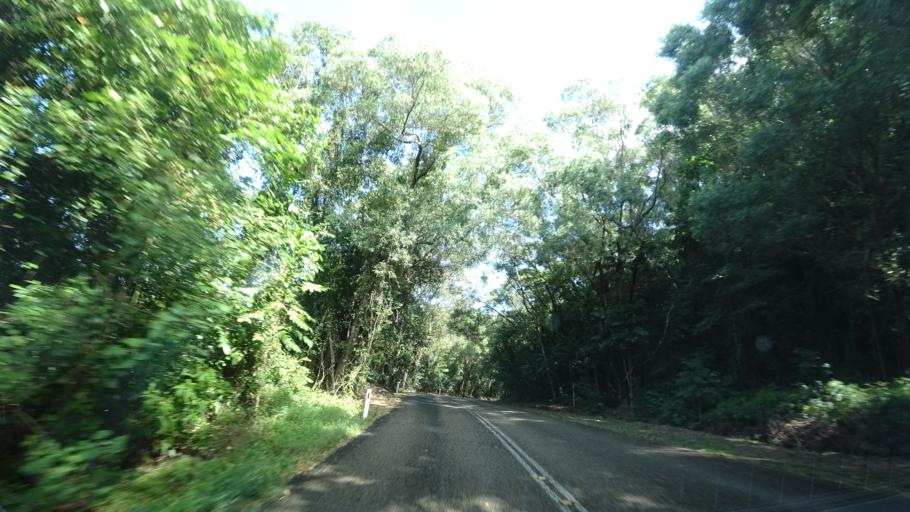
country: AU
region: Queensland
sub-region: Cairns
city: Port Douglas
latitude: -16.2572
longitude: 145.4378
